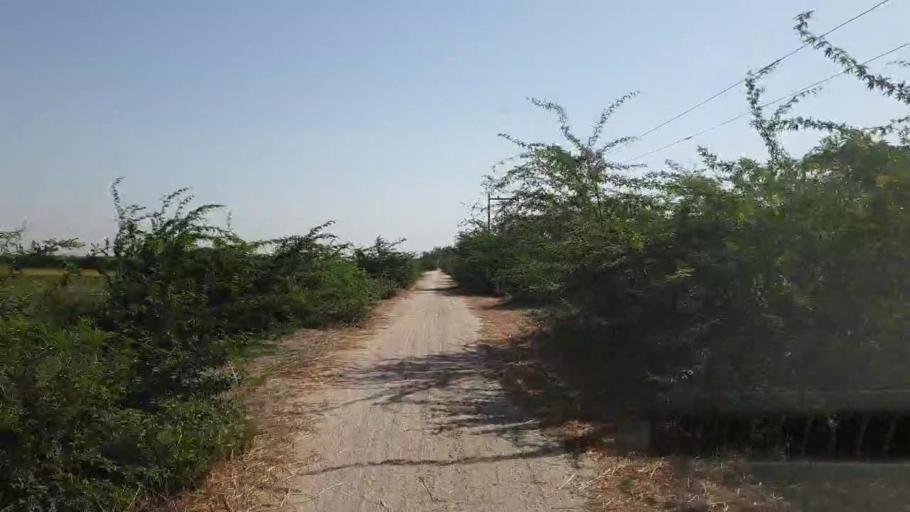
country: PK
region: Sindh
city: Tando Bago
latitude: 24.6435
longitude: 68.9878
